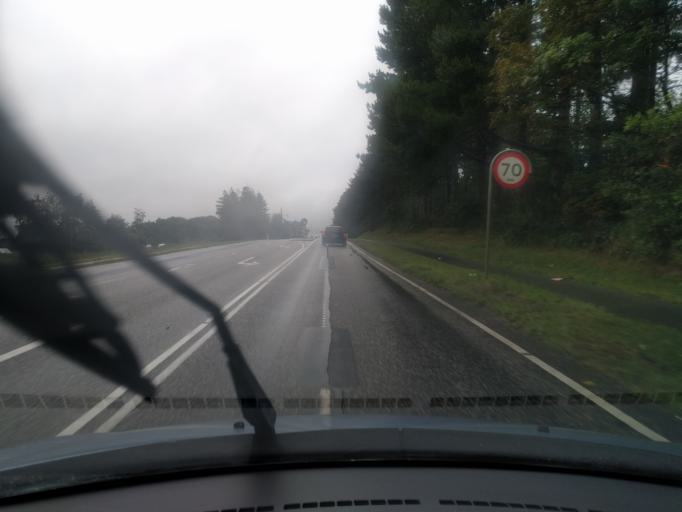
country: DK
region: Zealand
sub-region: Naestved Kommune
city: Naestved
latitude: 55.1750
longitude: 11.7992
